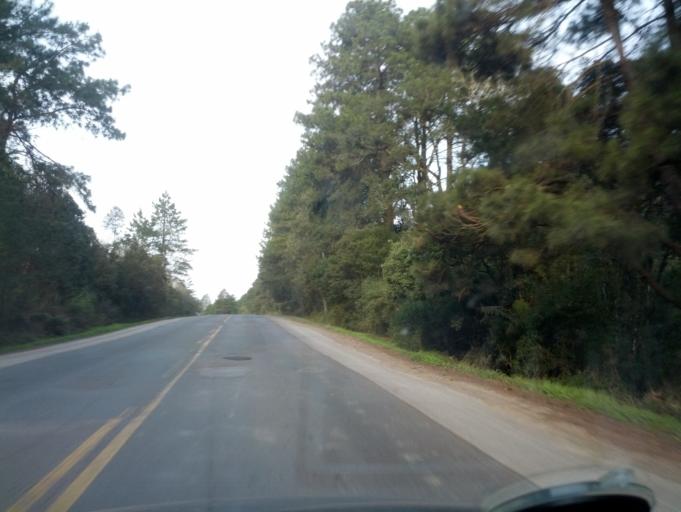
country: BR
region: Santa Catarina
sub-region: Otacilio Costa
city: Otacilio Costa
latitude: -27.3098
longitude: -50.1269
